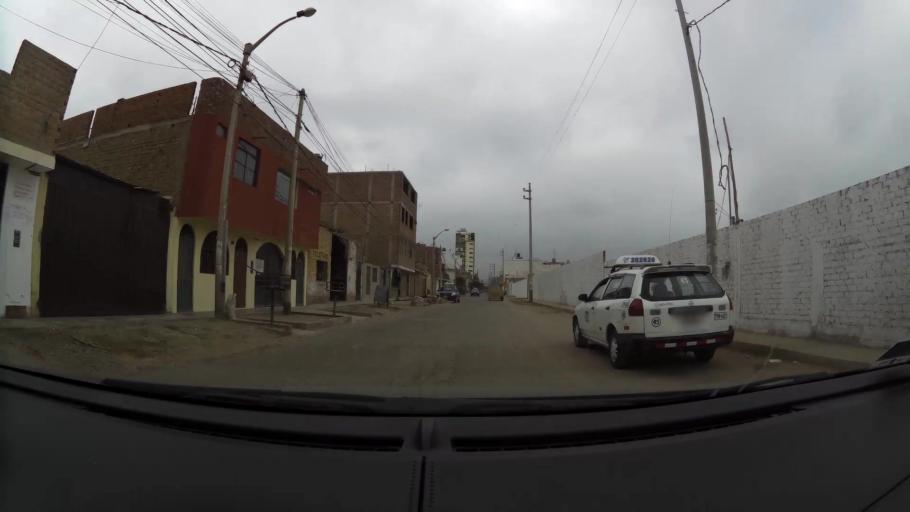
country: PE
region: La Libertad
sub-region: Provincia de Trujillo
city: Trujillo
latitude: -8.1216
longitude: -79.0462
